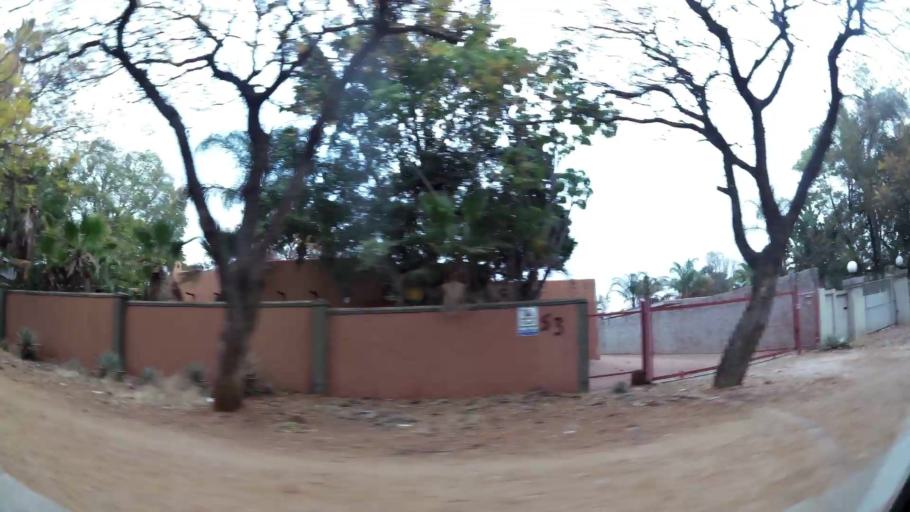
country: ZA
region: Limpopo
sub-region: Capricorn District Municipality
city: Polokwane
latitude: -23.9019
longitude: 29.4662
